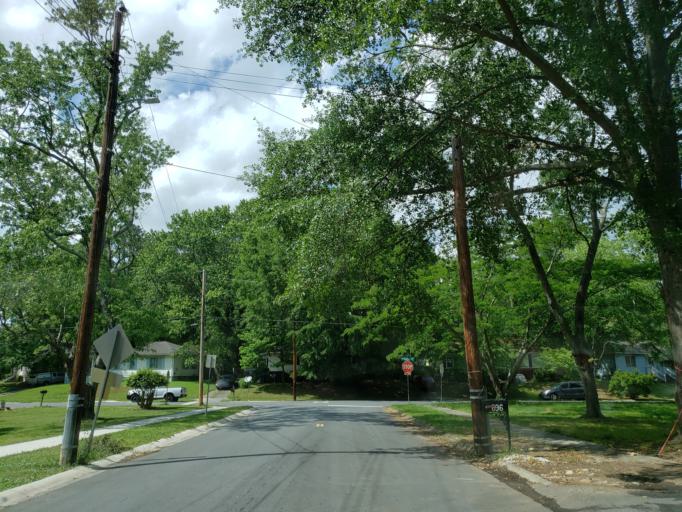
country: US
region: Georgia
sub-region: Cobb County
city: Smyrna
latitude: 33.8910
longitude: -84.5332
